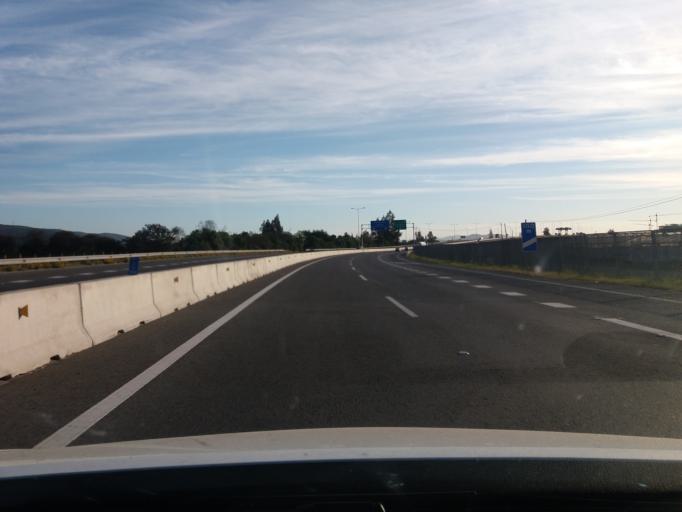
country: CL
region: Valparaiso
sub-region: Provincia de Quillota
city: Quillota
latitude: -32.8996
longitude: -71.2403
